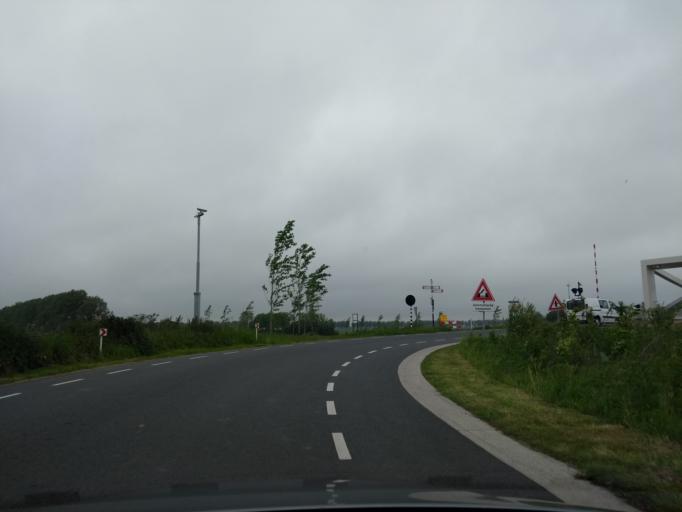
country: NL
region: Groningen
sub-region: Gemeente Zuidhorn
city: Aduard
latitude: 53.2581
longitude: 6.5018
